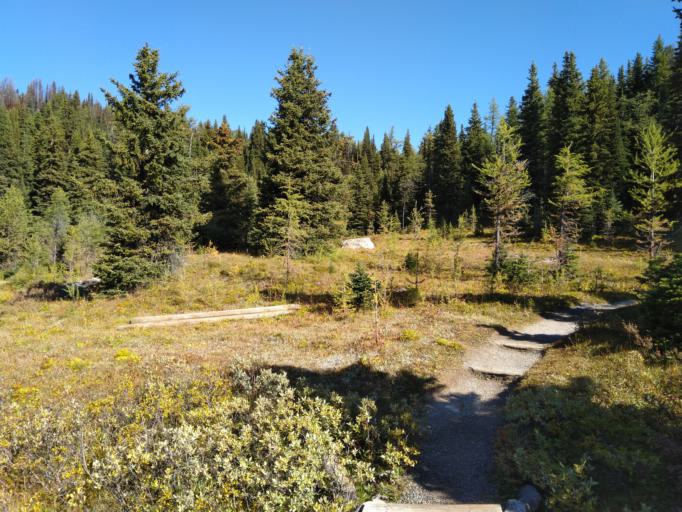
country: CA
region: Alberta
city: Banff
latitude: 51.0587
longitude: -115.7931
